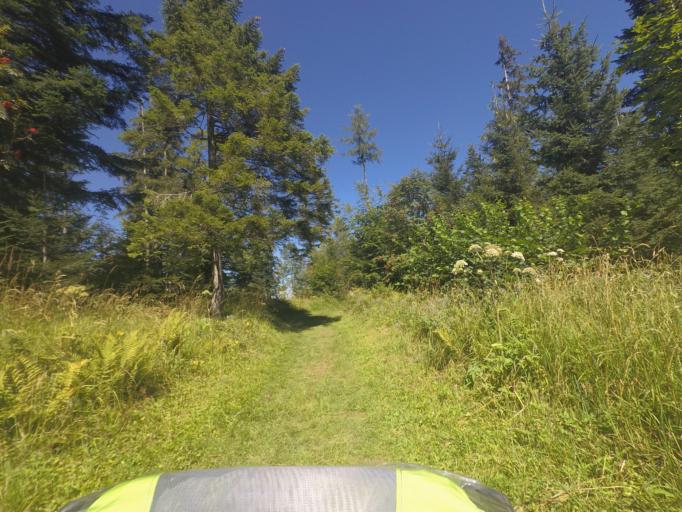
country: AT
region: Salzburg
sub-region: Politischer Bezirk Hallein
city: Hallein
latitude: 47.6508
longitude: 13.0991
